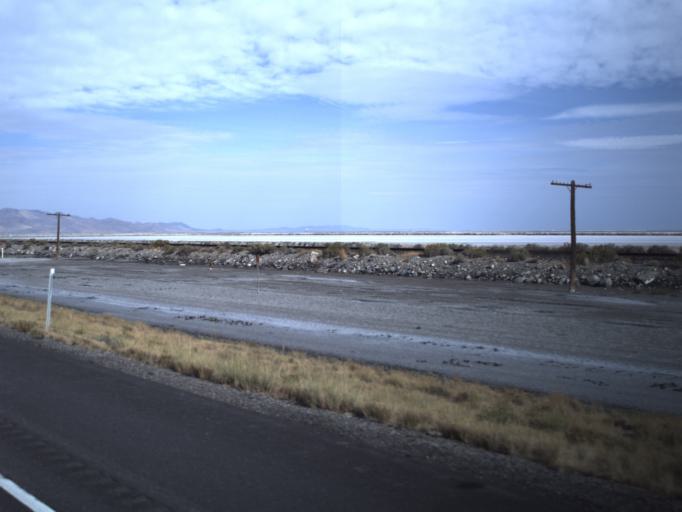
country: US
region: Utah
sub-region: Tooele County
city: Grantsville
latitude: 40.7232
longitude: -112.5638
